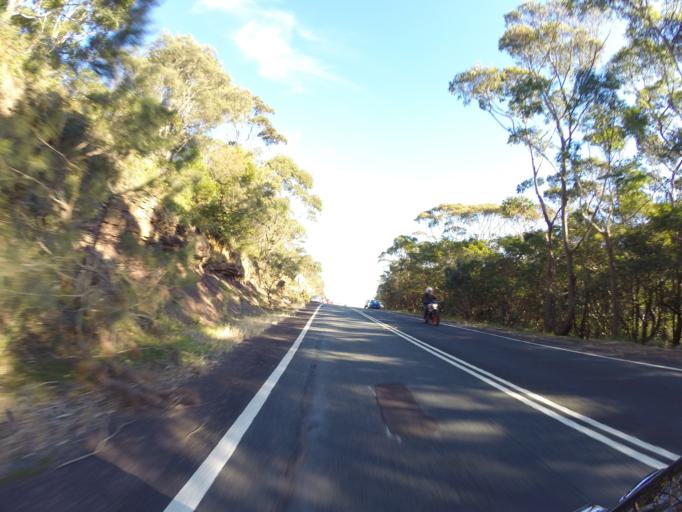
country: AU
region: New South Wales
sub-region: Wollongong
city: Helensburgh
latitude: -34.2102
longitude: 151.0114
